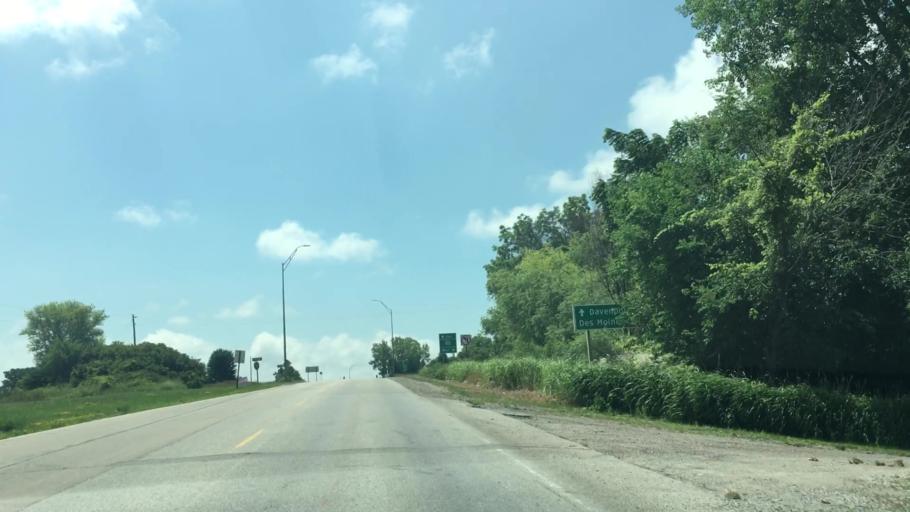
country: US
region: Iowa
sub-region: Johnson County
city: Tiffin
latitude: 41.6966
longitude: -91.6665
